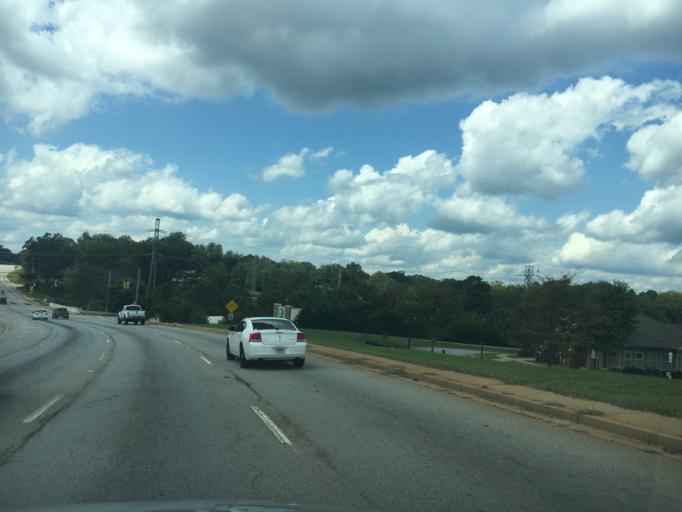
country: US
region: South Carolina
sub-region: Greenville County
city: Sans Souci
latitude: 34.8709
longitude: -82.4194
